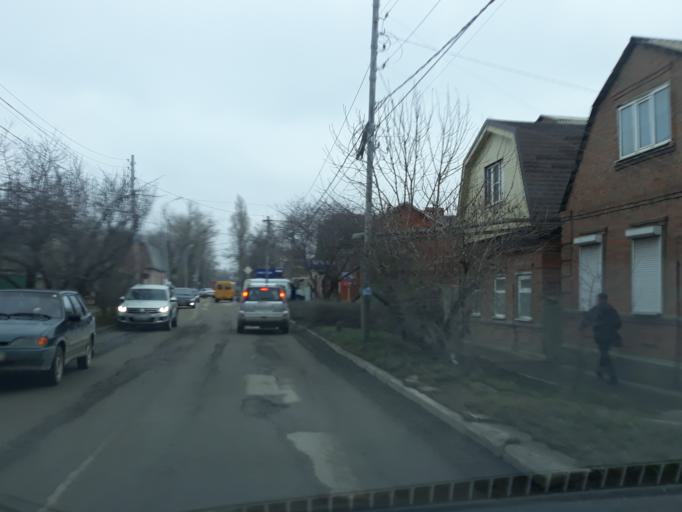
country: RU
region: Rostov
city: Taganrog
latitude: 47.2346
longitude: 38.9262
